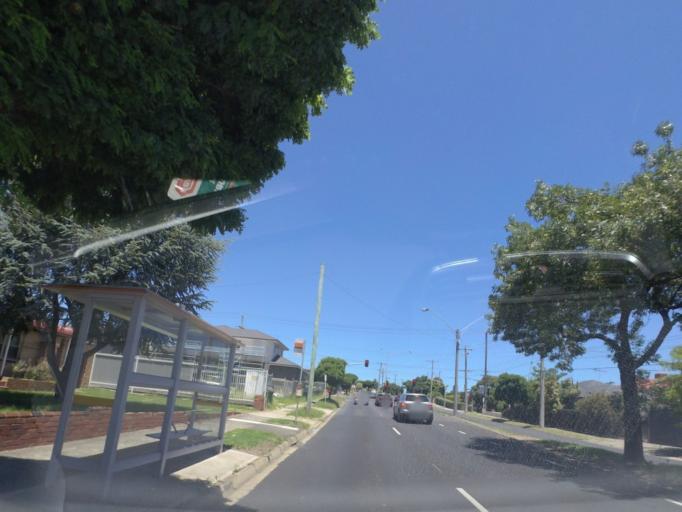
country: AU
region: Victoria
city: Heidelberg West
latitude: -37.7317
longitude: 145.0252
